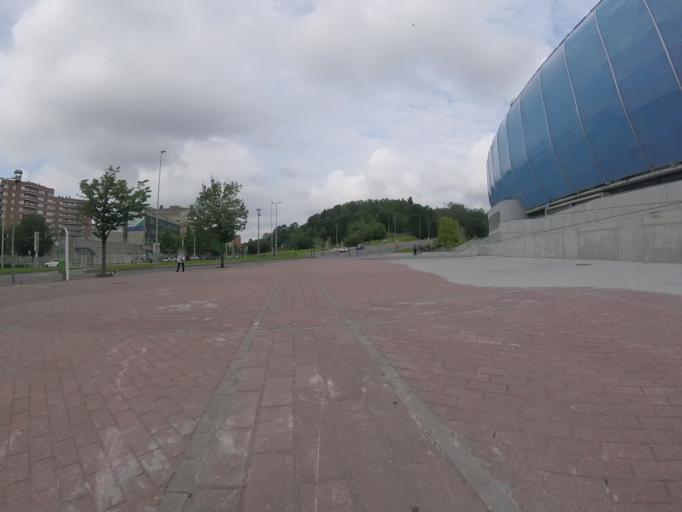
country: ES
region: Basque Country
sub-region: Provincia de Guipuzcoa
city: San Sebastian
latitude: 43.3024
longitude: -1.9744
